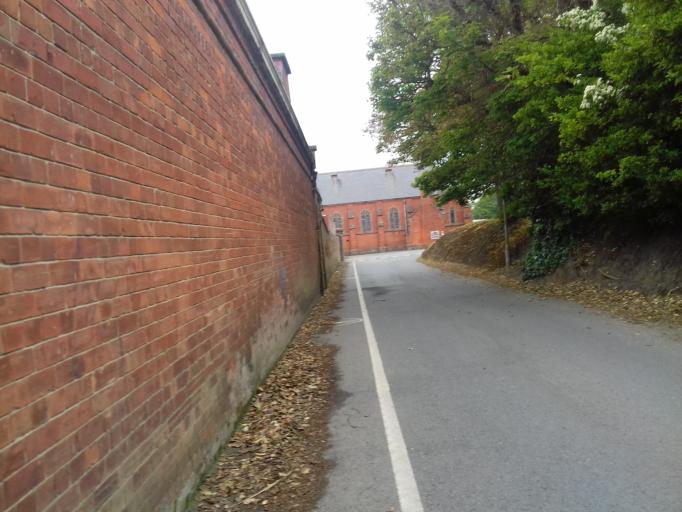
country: IE
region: Leinster
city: Portraine
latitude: 53.4871
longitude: -6.1110
